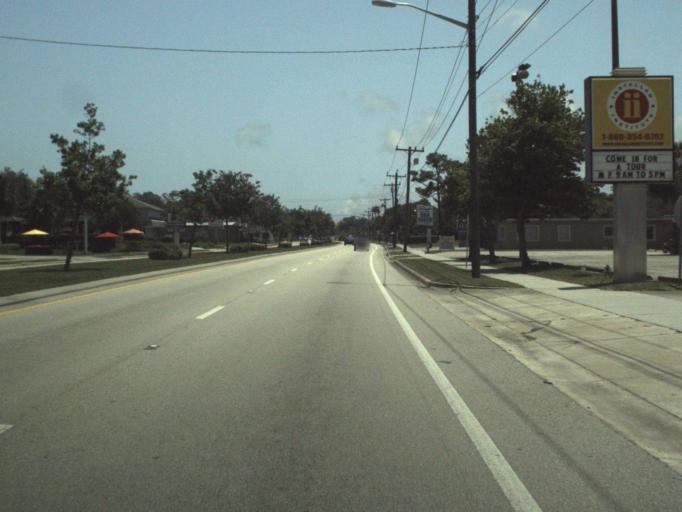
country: US
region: Florida
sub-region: Volusia County
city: Holly Hill
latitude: 29.2549
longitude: -81.0465
